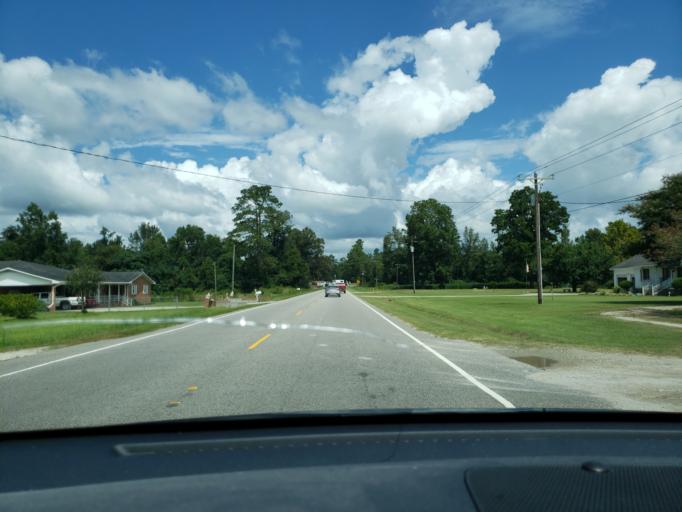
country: US
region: North Carolina
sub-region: Columbus County
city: Brunswick
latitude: 34.2452
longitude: -78.7546
